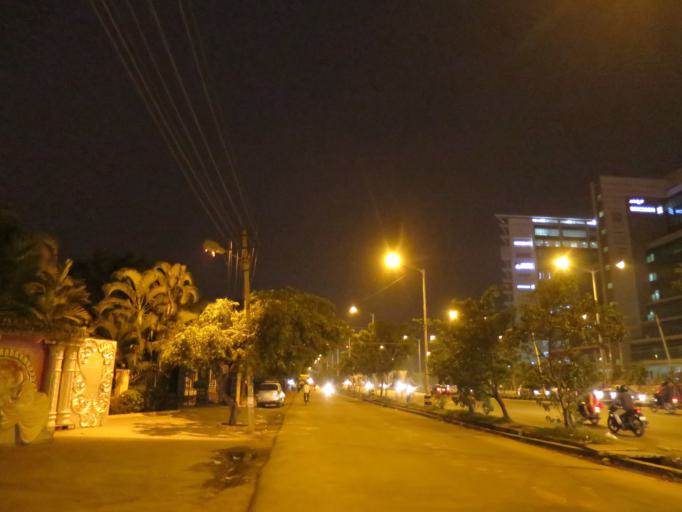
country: IN
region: Karnataka
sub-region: Bangalore Urban
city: Bangalore
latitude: 12.9822
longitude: 77.6929
